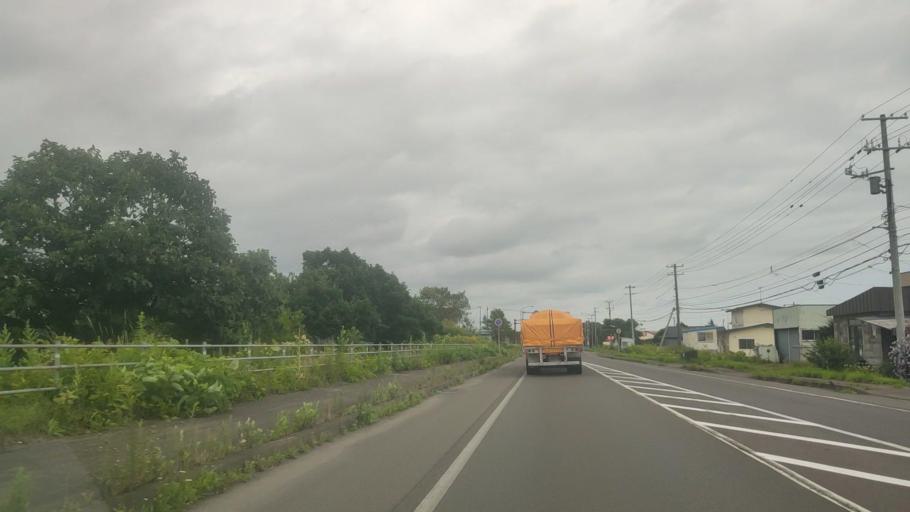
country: JP
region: Hokkaido
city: Shiraoi
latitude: 42.5231
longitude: 141.3127
